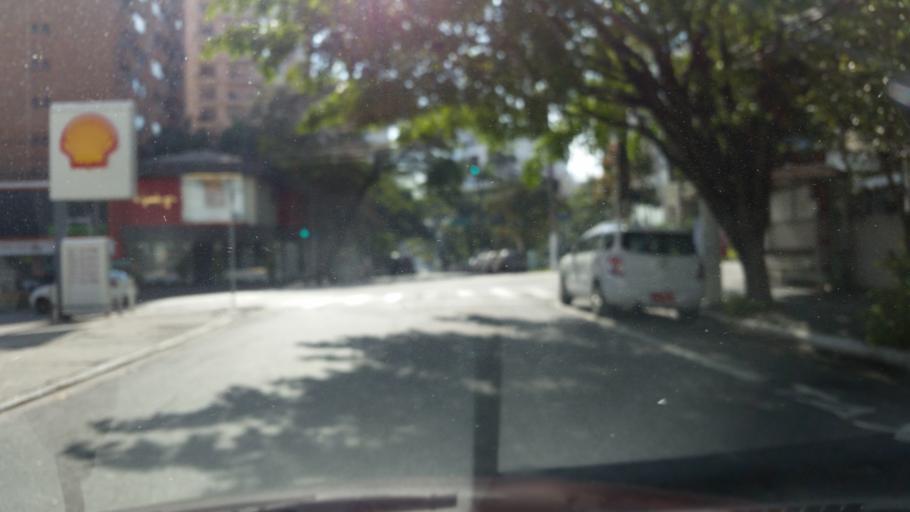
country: BR
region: Sao Paulo
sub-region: Diadema
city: Diadema
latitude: -23.6235
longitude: -46.6825
